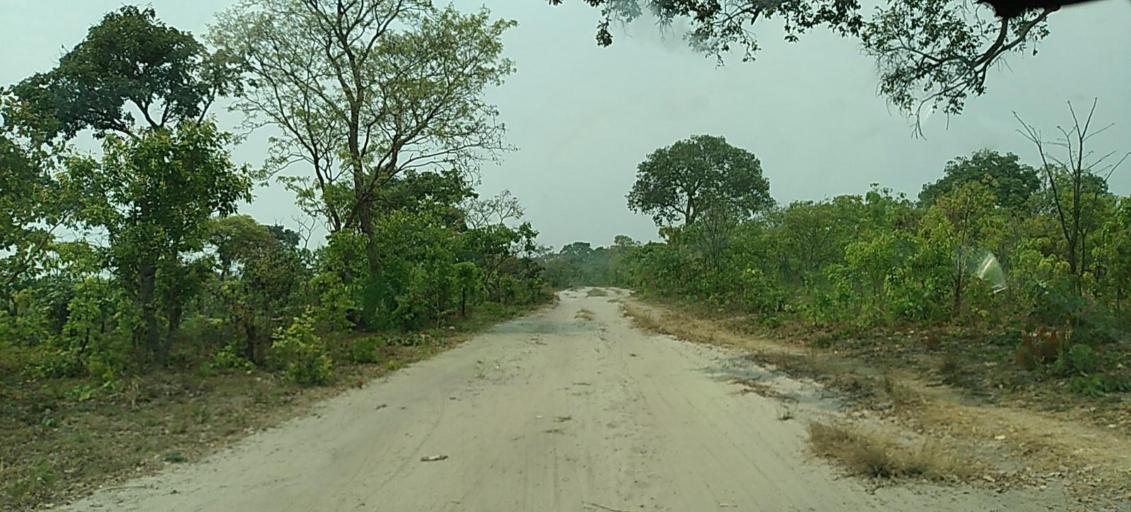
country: ZM
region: North-Western
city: Kabompo
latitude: -13.4758
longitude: 24.4546
